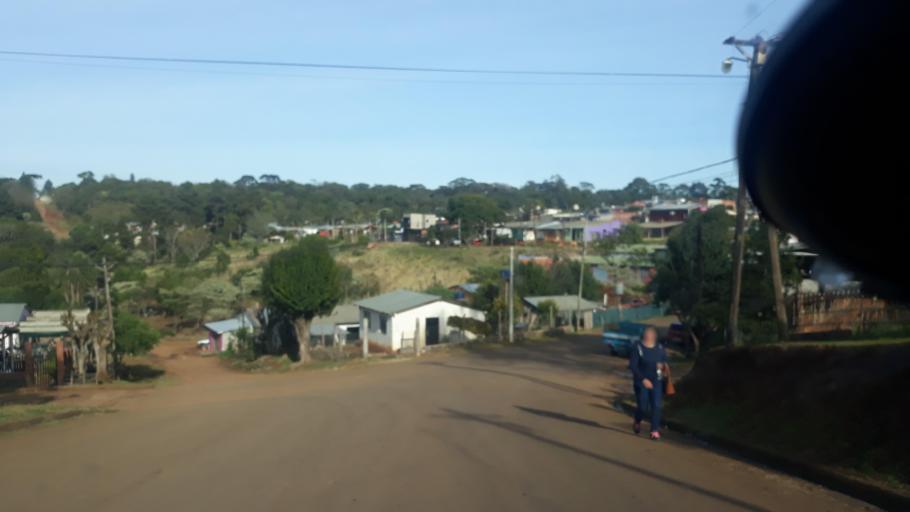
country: AR
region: Misiones
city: Bernardo de Irigoyen
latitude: -26.2655
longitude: -53.6522
